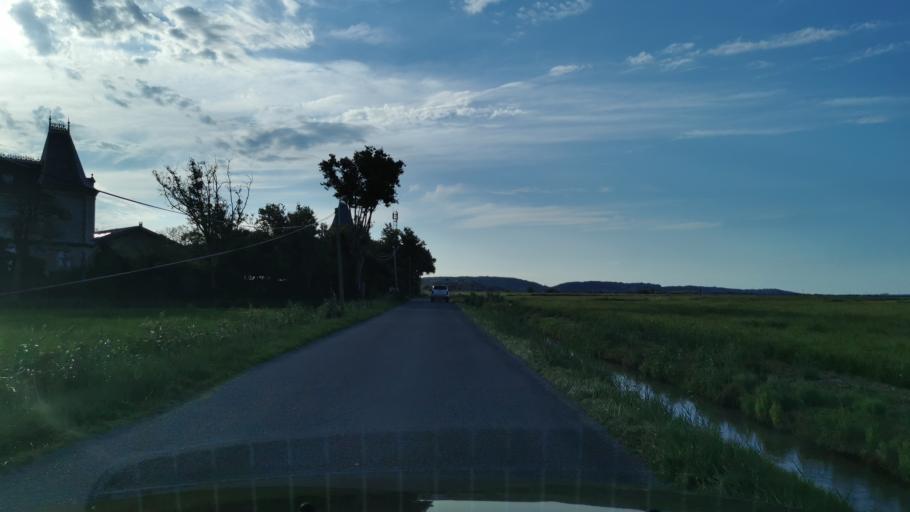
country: FR
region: Languedoc-Roussillon
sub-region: Departement de l'Aude
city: Gruissan
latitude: 43.1204
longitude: 3.0342
